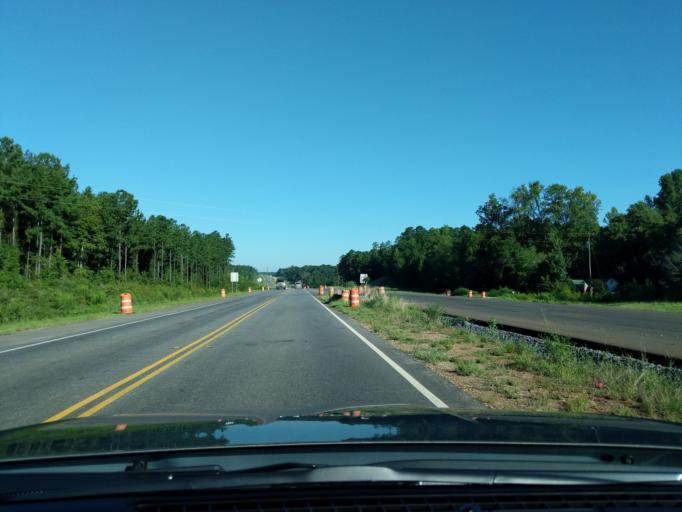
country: US
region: Georgia
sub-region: McDuffie County
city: Thomson
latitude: 33.5777
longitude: -82.5254
